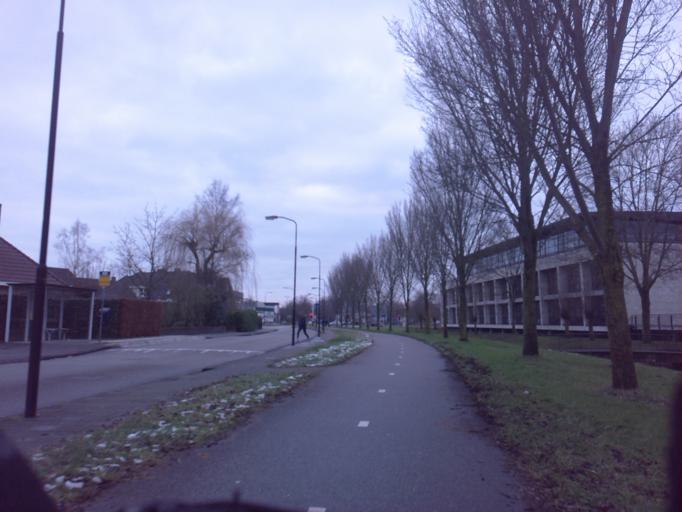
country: NL
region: Utrecht
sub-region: Gemeente Leusden
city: Leusden
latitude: 52.1441
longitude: 5.4240
